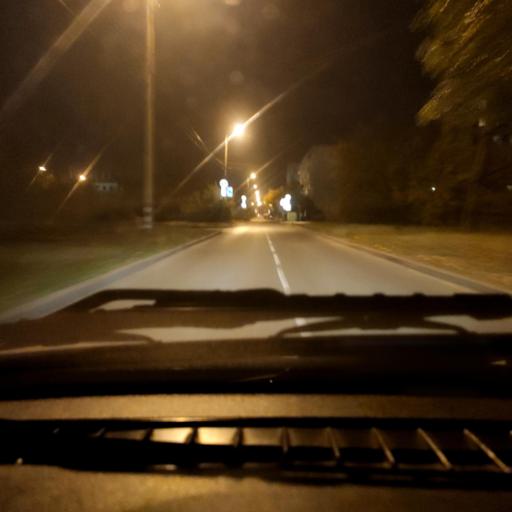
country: RU
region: Samara
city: Zhigulevsk
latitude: 53.4741
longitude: 49.5323
